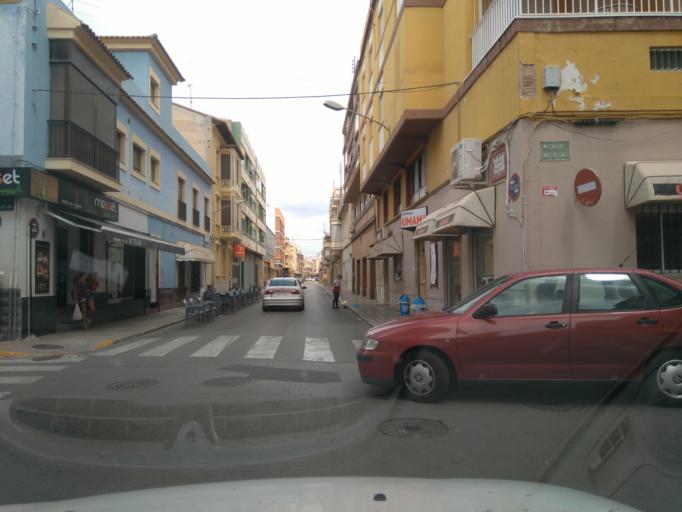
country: ES
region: Valencia
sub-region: Provincia de Valencia
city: Carcaixent
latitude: 39.1222
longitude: -0.4474
